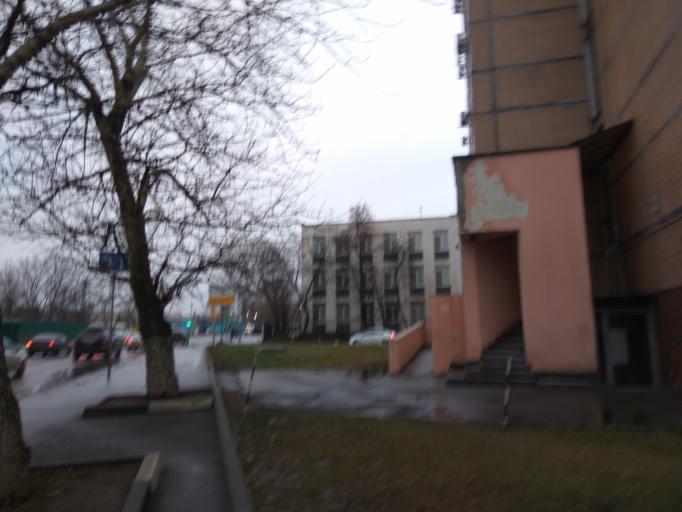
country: RU
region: Moscow
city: Tekstil'shchiki
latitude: 55.7046
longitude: 37.7270
